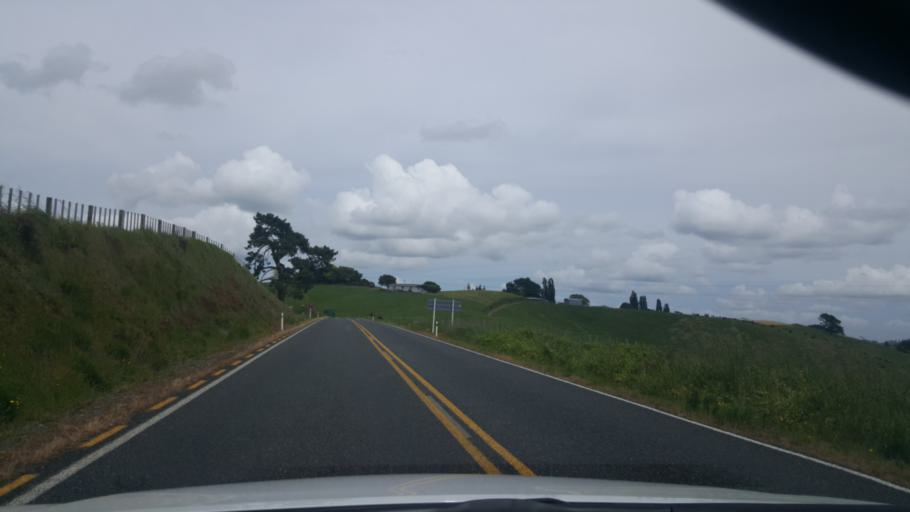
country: NZ
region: Waikato
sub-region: Matamata-Piako District
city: Matamata
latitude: -37.8740
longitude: 175.6857
